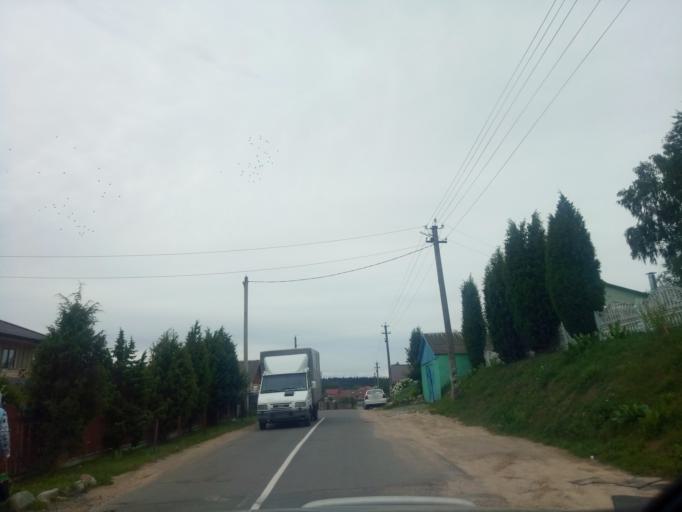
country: BY
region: Minsk
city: Zhdanovichy
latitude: 53.9263
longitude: 27.3839
